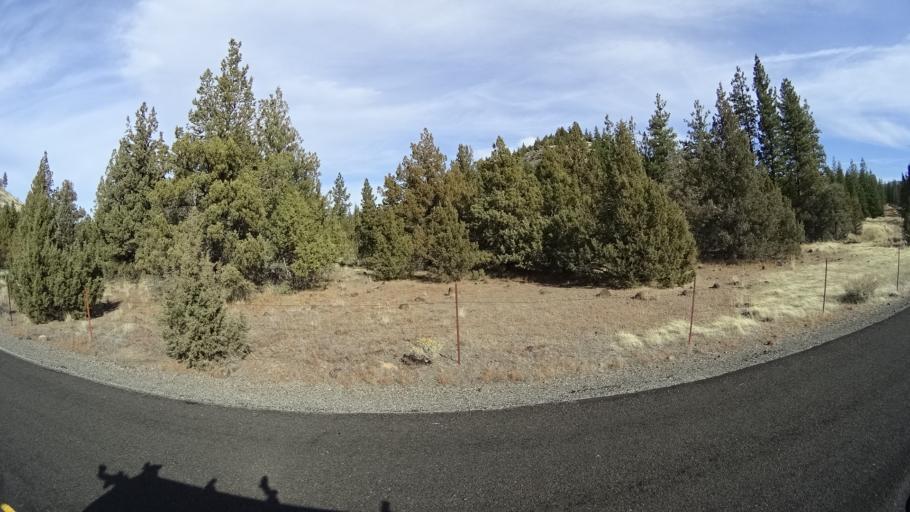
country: US
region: California
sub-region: Siskiyou County
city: Weed
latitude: 41.4981
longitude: -122.3888
